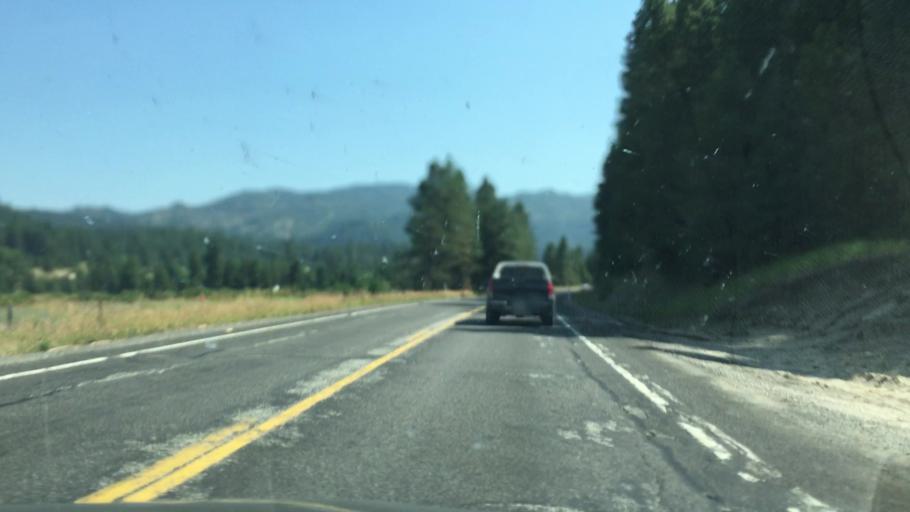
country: US
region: Idaho
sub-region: Valley County
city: Cascade
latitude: 44.2904
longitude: -116.0814
